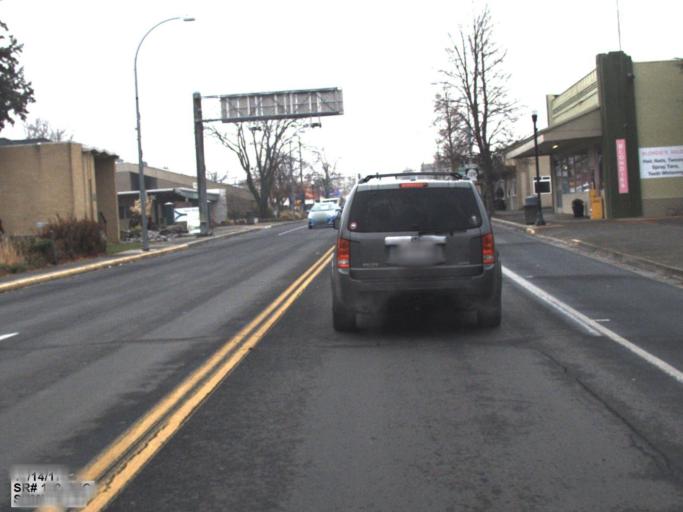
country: US
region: Washington
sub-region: Asotin County
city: Clarkston
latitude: 46.4158
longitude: -117.0456
